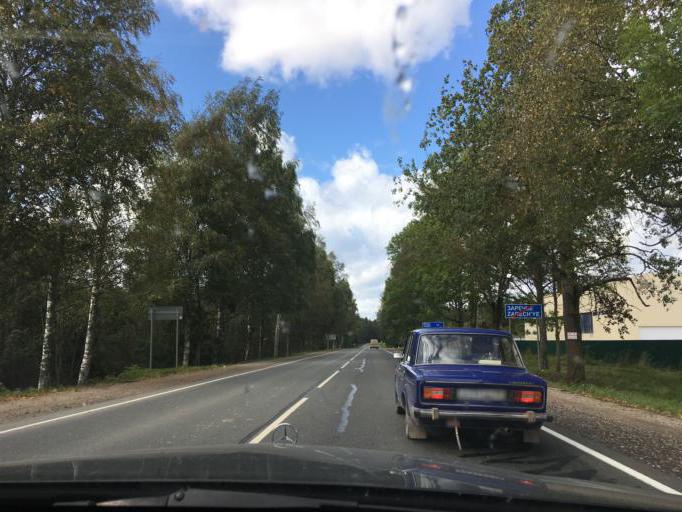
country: RU
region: Pskov
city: Pustoshka
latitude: 56.4024
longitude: 29.2257
